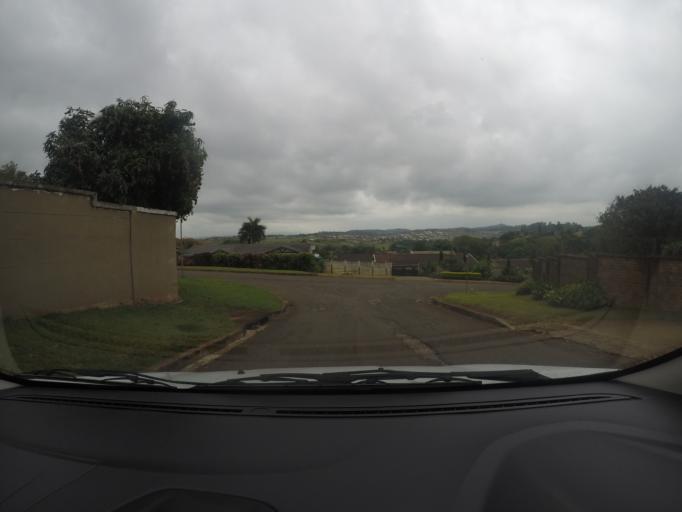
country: ZA
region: KwaZulu-Natal
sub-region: uThungulu District Municipality
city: Empangeni
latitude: -28.7635
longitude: 31.8894
